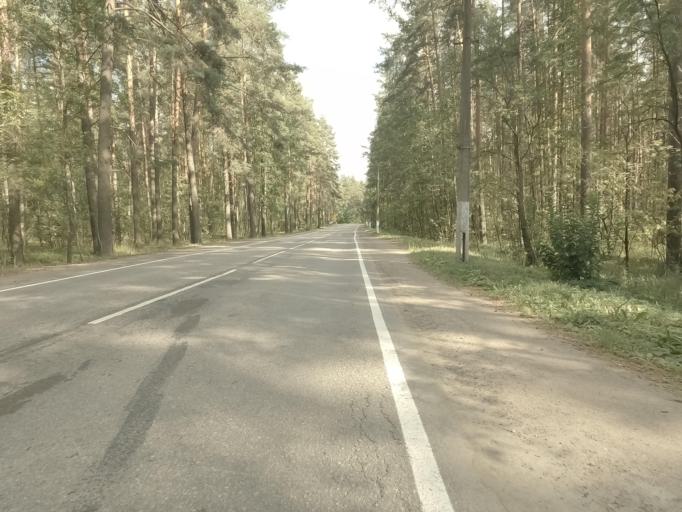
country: RU
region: Leningrad
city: Kamennogorsk
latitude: 60.9445
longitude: 29.1463
